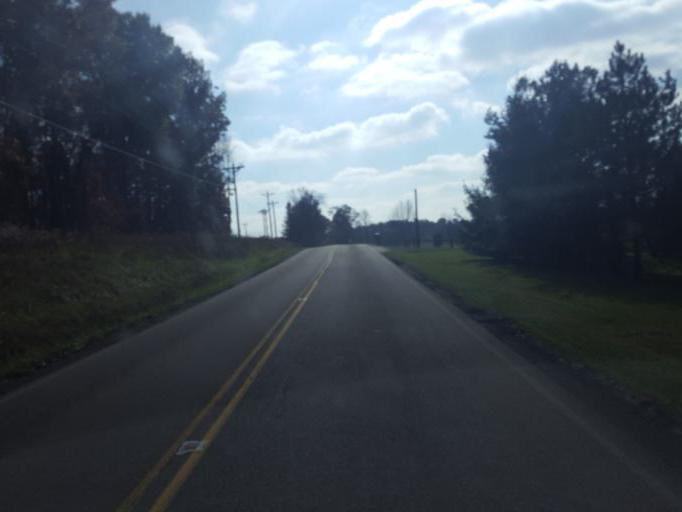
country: US
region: Ohio
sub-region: Knox County
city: Oak Hill
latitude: 40.4594
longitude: -82.1302
